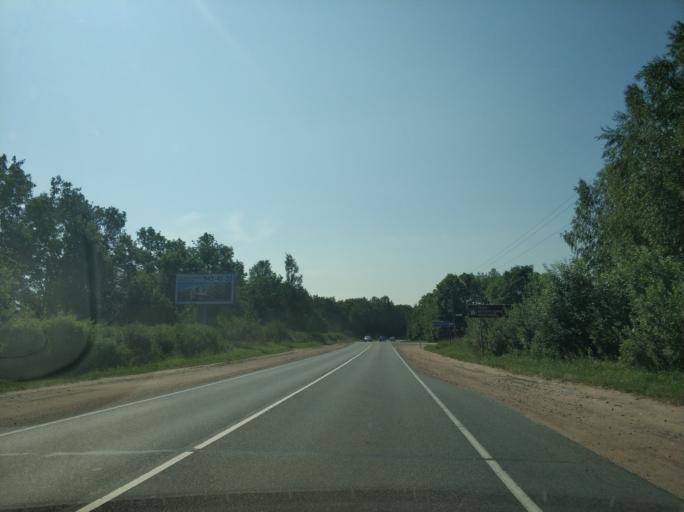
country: RU
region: Leningrad
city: Romanovka
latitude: 60.0613
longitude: 30.7422
